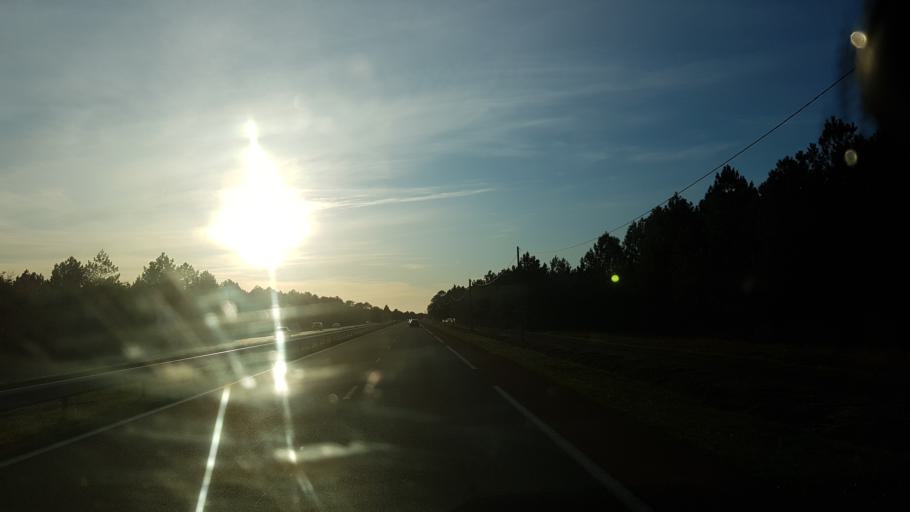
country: FR
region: Aquitaine
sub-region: Departement de la Gironde
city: Marcheprime
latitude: 44.7858
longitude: -0.9157
